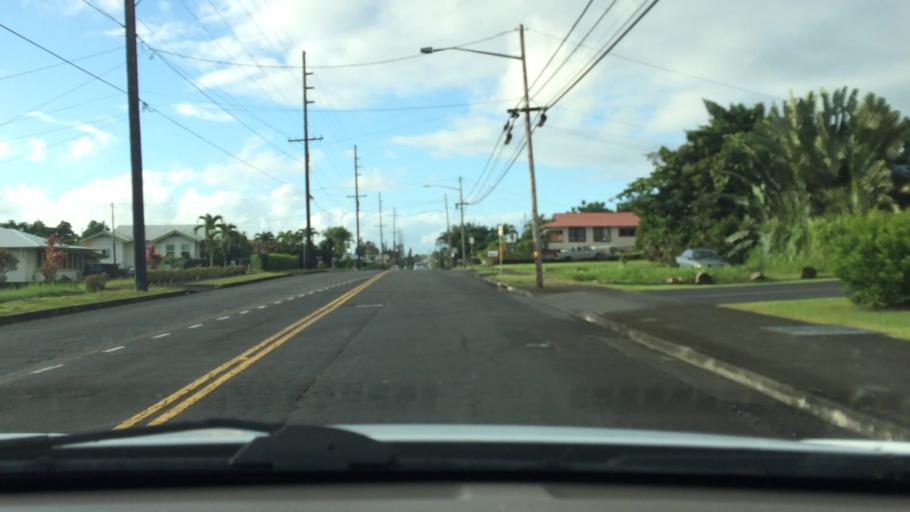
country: US
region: Hawaii
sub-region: Hawaii County
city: Hilo
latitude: 19.7055
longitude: -155.0764
